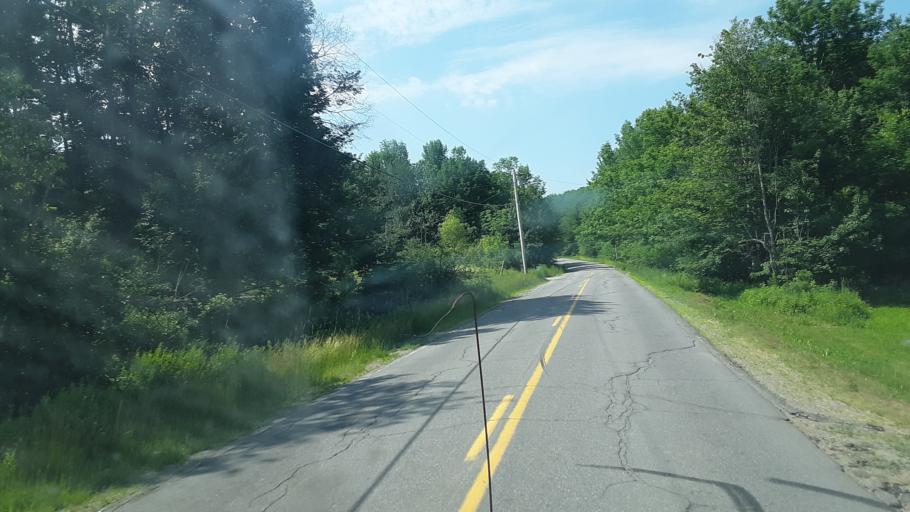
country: US
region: Maine
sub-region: Waldo County
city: Swanville
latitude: 44.5716
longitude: -68.9512
